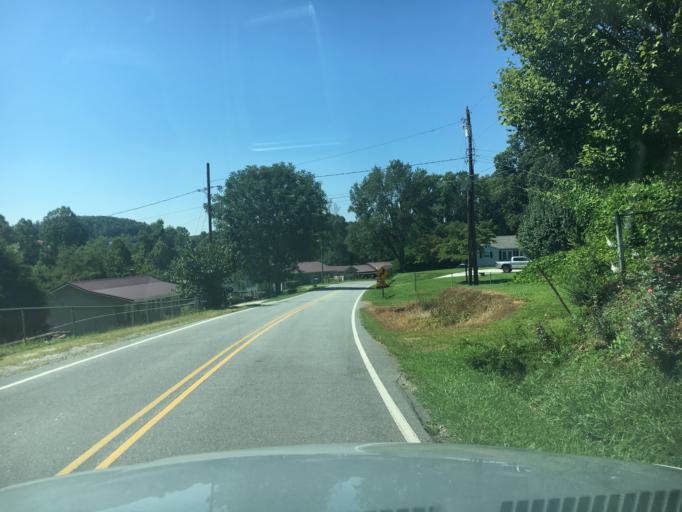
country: US
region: North Carolina
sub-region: McDowell County
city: West Marion
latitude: 35.6694
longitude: -82.0272
